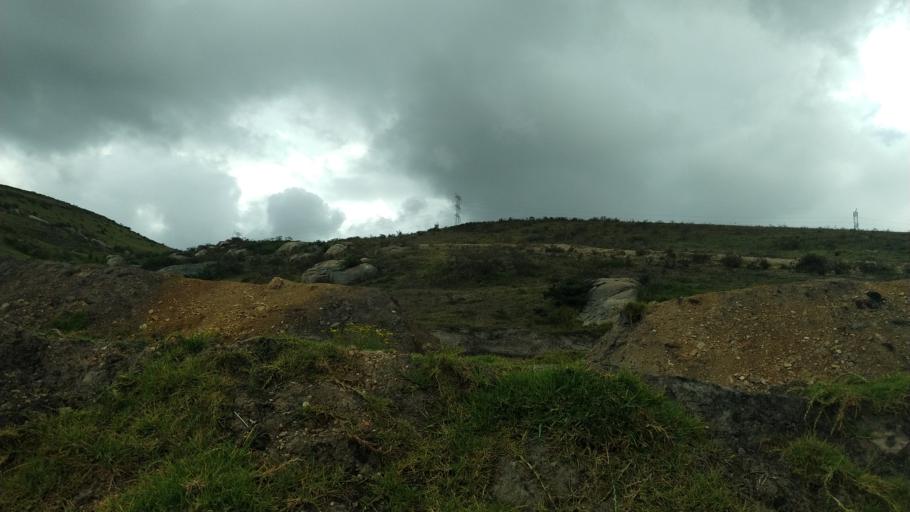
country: CO
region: Cundinamarca
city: Soacha
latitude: 4.5616
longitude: -74.1886
